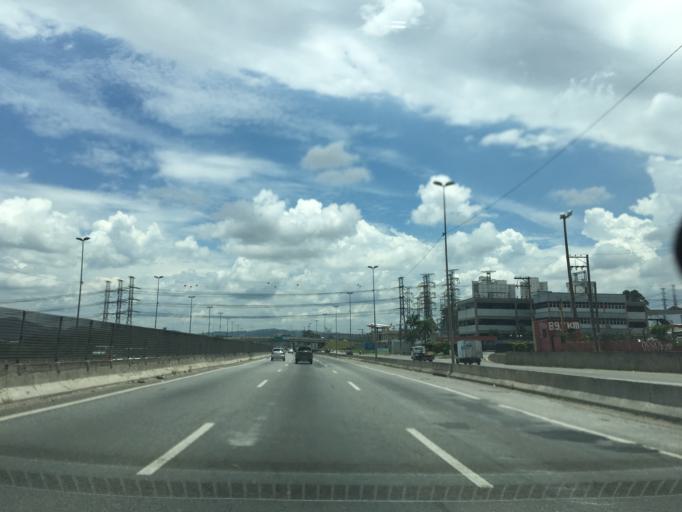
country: BR
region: Sao Paulo
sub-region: Guarulhos
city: Guarulhos
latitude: -23.4907
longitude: -46.5593
